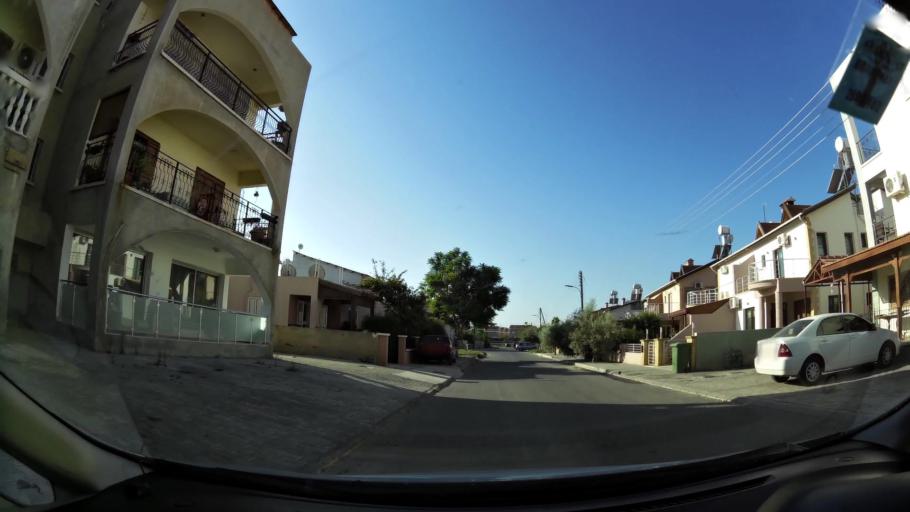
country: CY
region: Lefkosia
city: Nicosia
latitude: 35.2116
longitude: 33.2943
